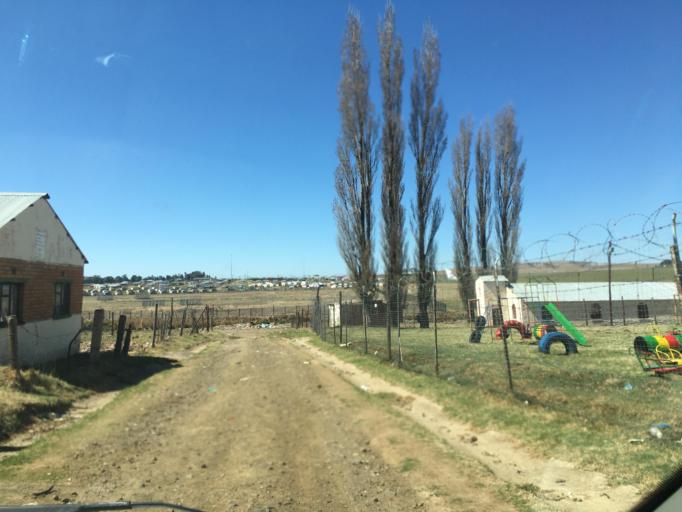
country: ZA
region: Eastern Cape
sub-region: Chris Hani District Municipality
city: Elliot
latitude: -31.3312
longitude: 27.8257
